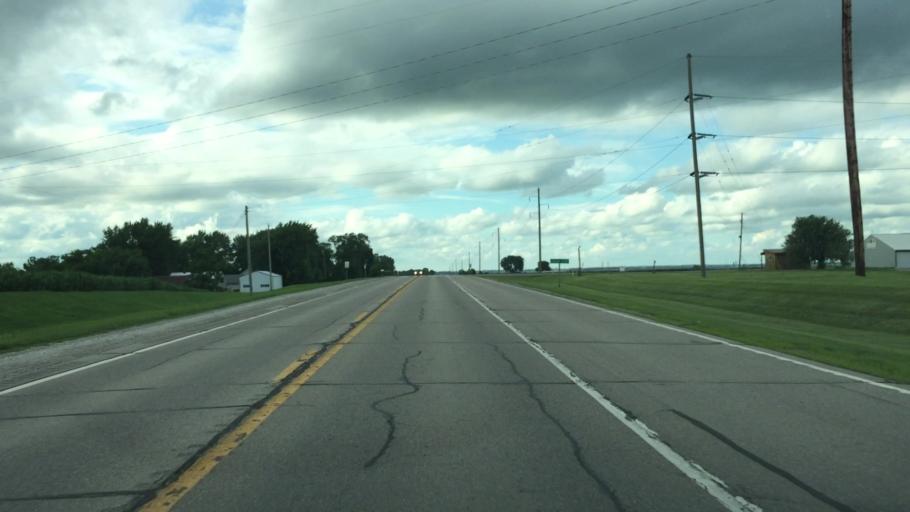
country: US
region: Iowa
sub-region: Jasper County
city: Monroe
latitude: 41.5719
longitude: -93.0970
